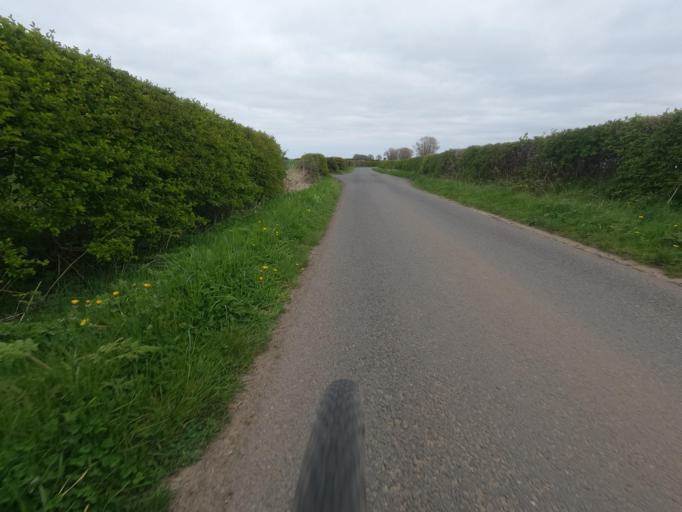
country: GB
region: England
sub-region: Northumberland
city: Darras Hall
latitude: 55.0772
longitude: -1.7931
